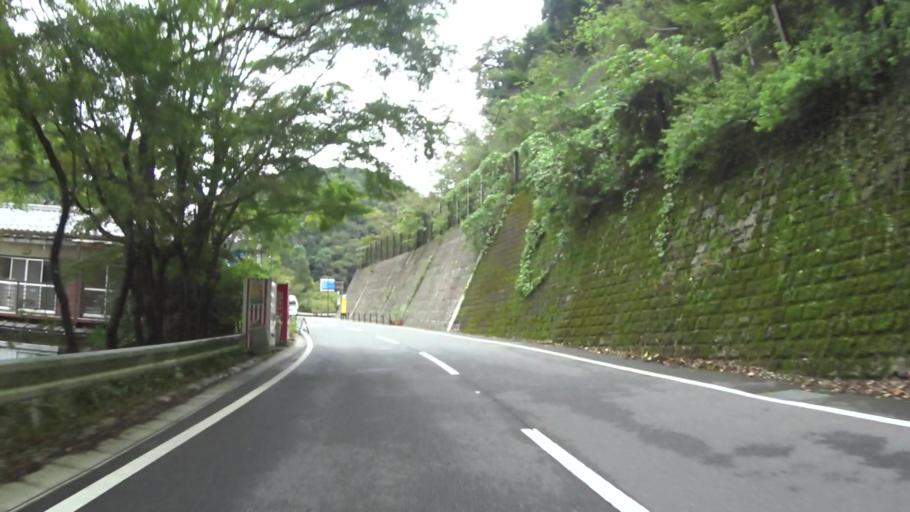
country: JP
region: Kyoto
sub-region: Kyoto-shi
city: Kamigyo-ku
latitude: 35.1039
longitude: 135.7638
